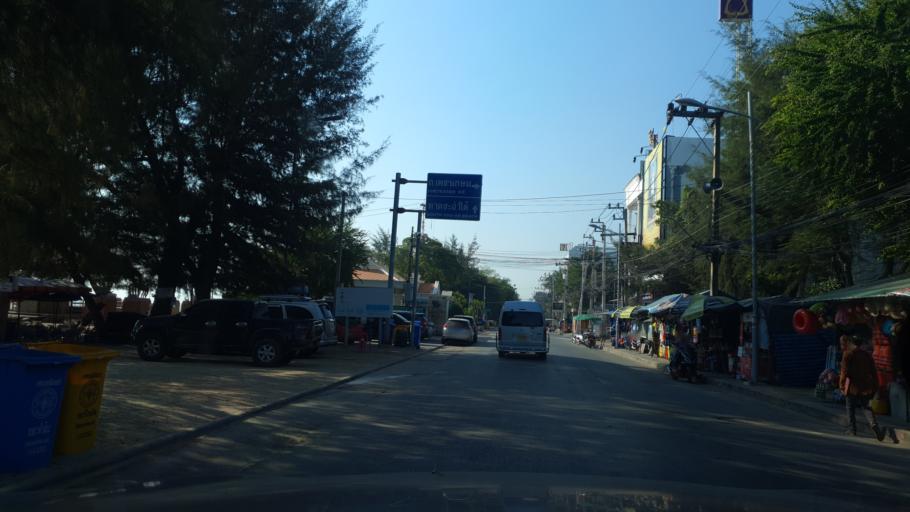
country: TH
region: Phetchaburi
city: Cha-am
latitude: 12.7951
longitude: 99.9840
